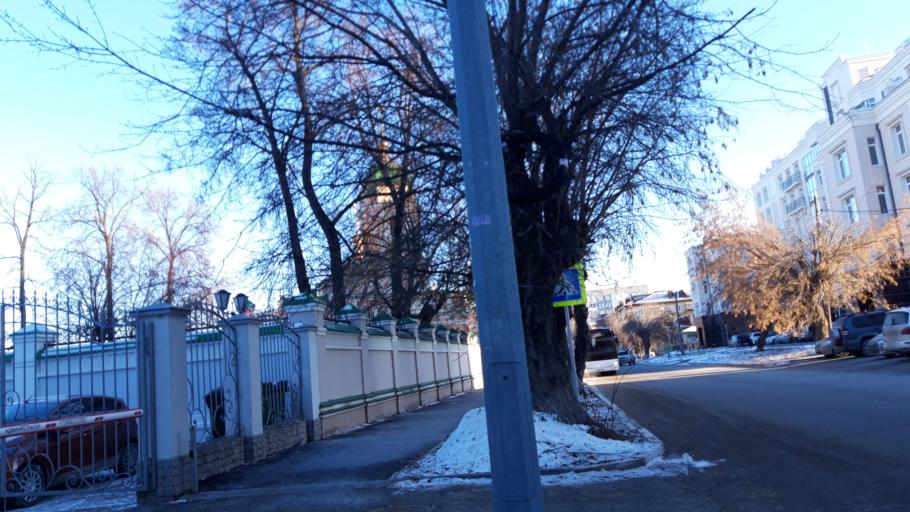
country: RU
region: Tjumen
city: Tyumen
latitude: 57.1605
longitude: 65.5472
